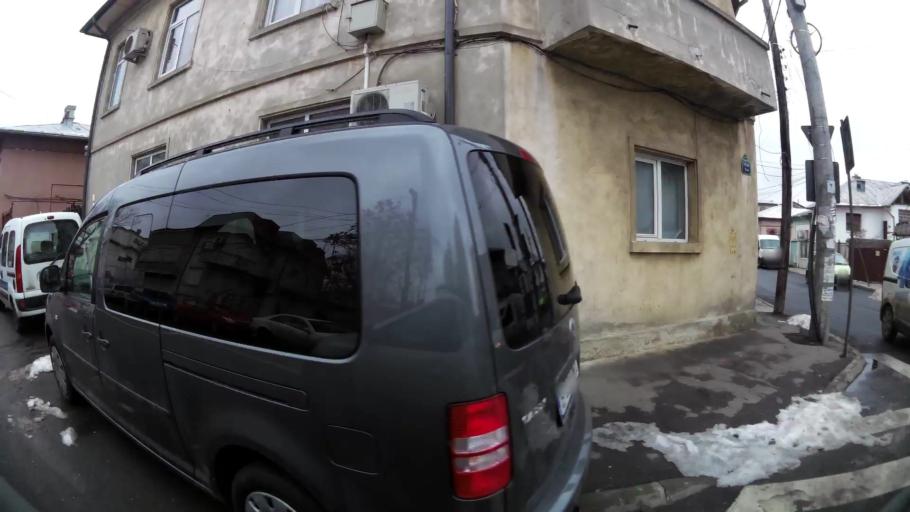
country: RO
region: Bucuresti
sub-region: Municipiul Bucuresti
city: Bucuresti
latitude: 44.4573
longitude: 26.0692
